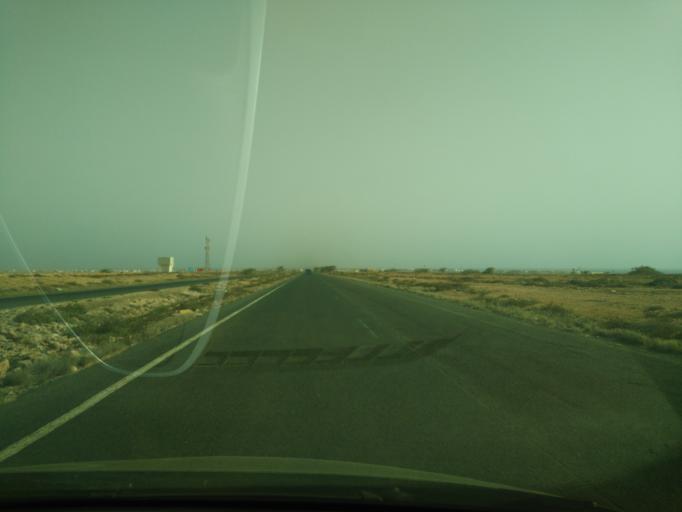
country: CV
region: Sal
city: Santa Maria
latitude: 16.6397
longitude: -22.9172
